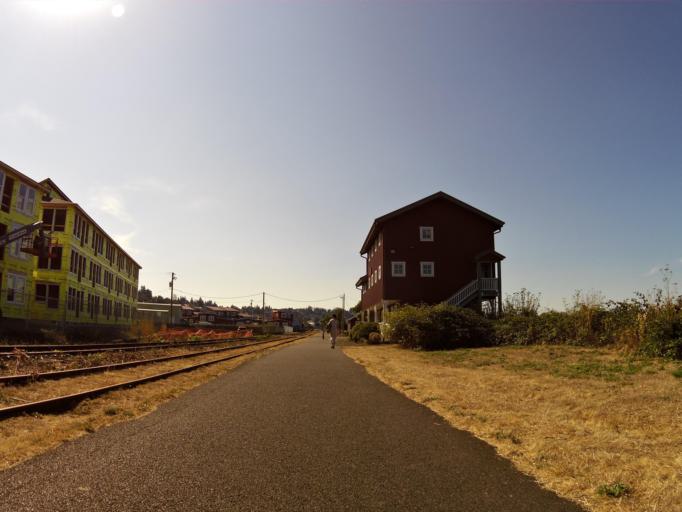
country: US
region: Oregon
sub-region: Clatsop County
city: Astoria
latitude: 46.1926
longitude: -123.8097
